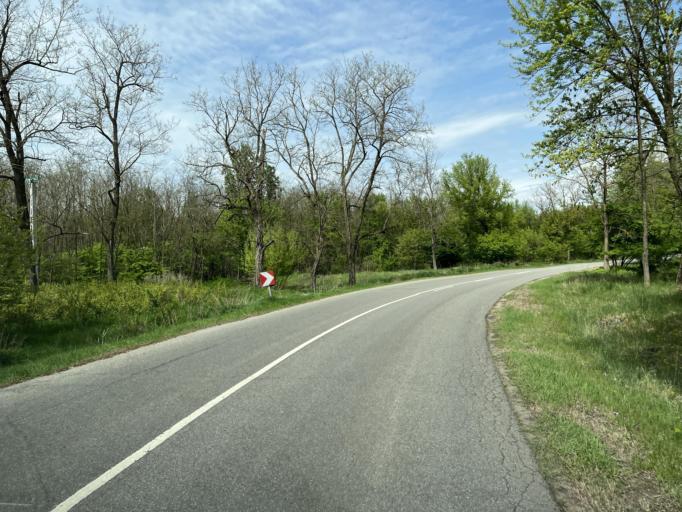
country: HU
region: Pest
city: Albertirsa
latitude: 47.1583
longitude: 19.6113
